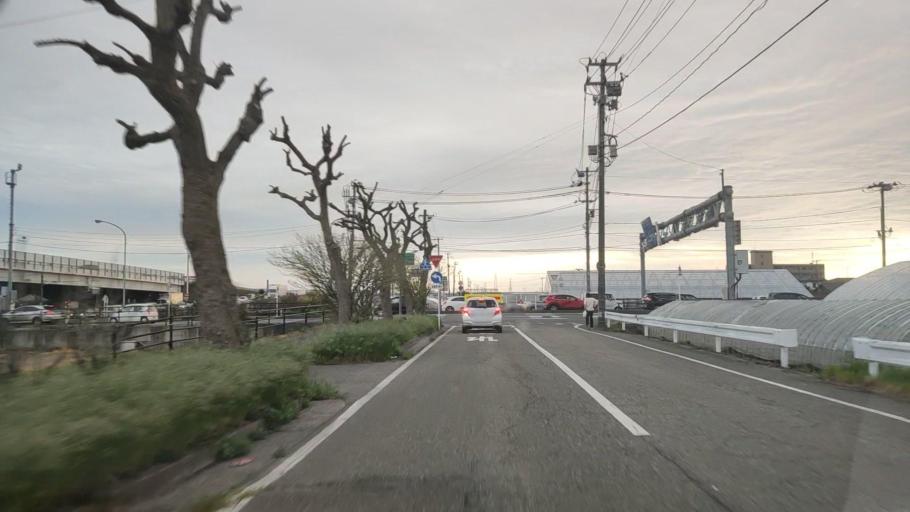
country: JP
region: Niigata
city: Kameda-honcho
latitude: 37.9130
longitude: 139.0982
